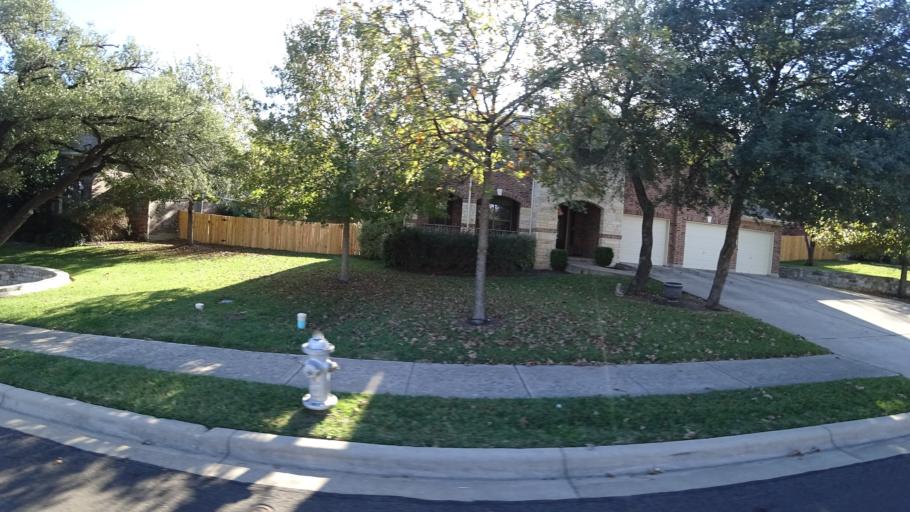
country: US
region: Texas
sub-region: Travis County
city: Barton Creek
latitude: 30.2481
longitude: -97.8745
